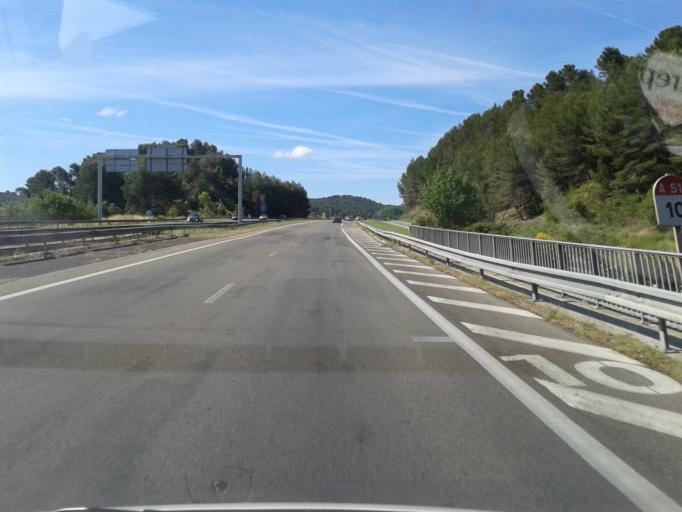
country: FR
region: Provence-Alpes-Cote d'Azur
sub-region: Departement des Bouches-du-Rhone
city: Bouc-Bel-Air
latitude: 43.4678
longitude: 5.4071
